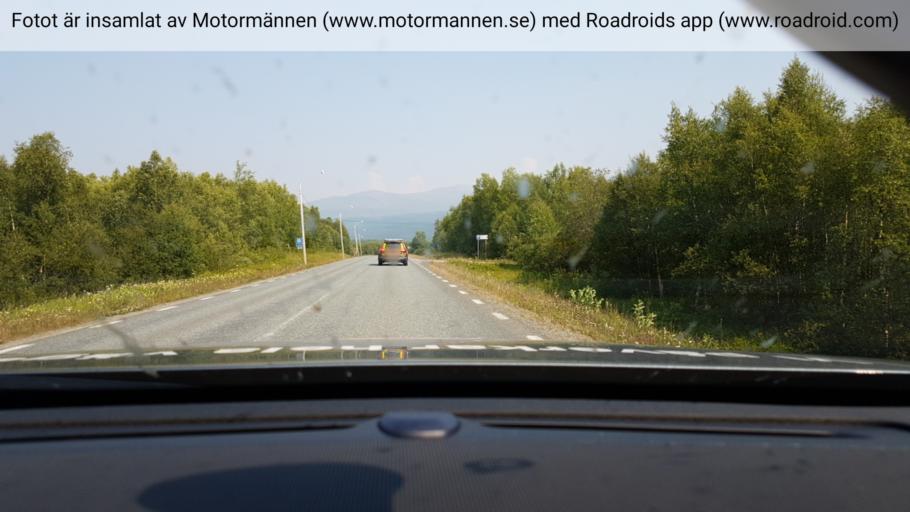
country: NO
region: Nordland
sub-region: Rana
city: Mo i Rana
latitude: 65.7720
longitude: 15.1121
